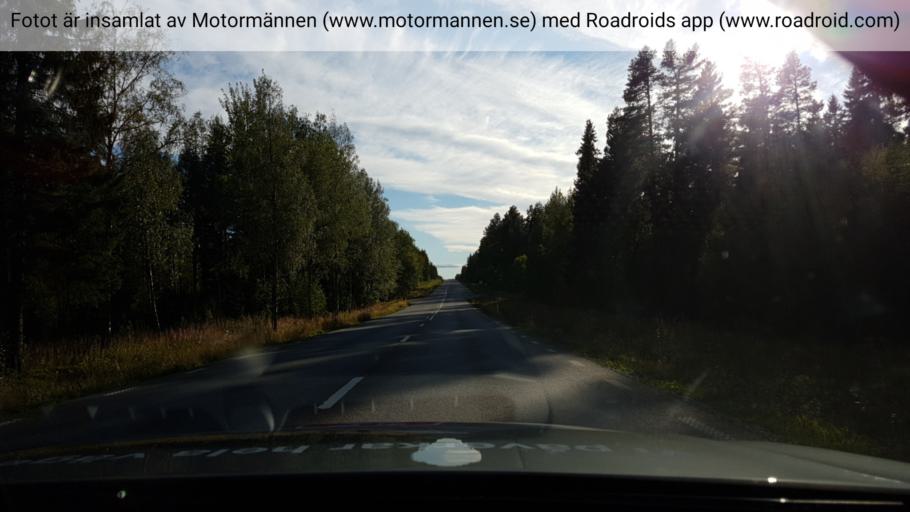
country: SE
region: Jaemtland
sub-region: OEstersunds Kommun
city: Lit
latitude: 63.2547
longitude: 14.8187
